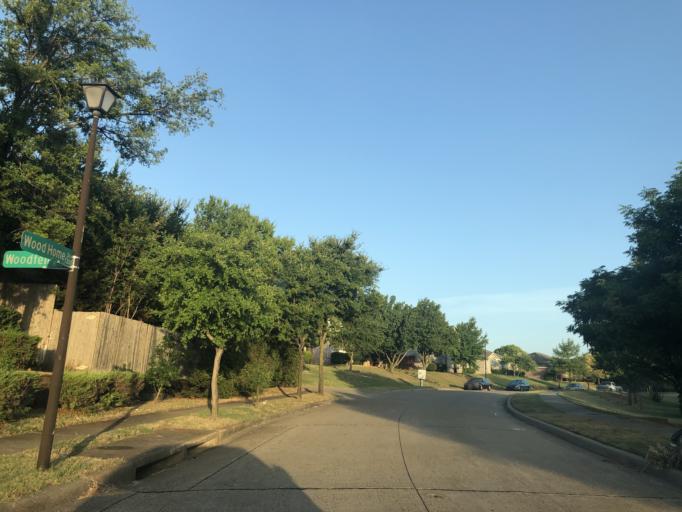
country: US
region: Texas
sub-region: Dallas County
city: Duncanville
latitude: 32.6473
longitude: -96.9524
